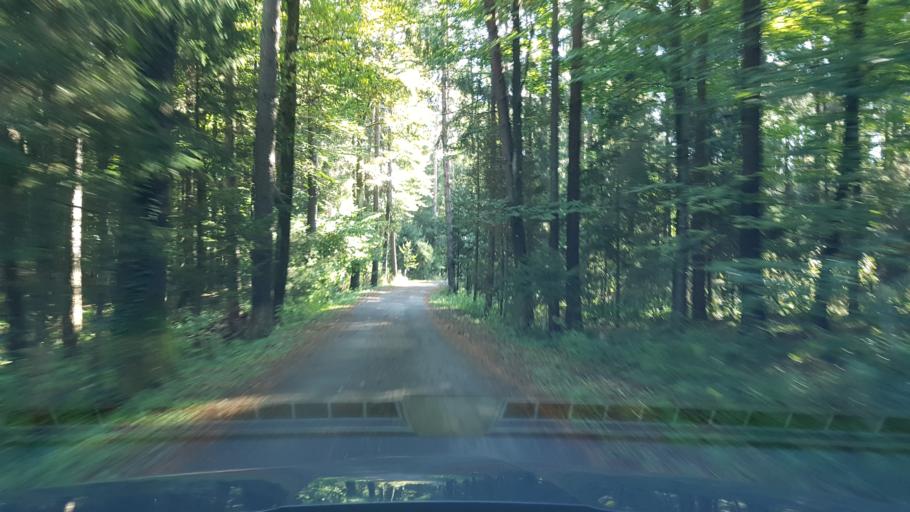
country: AT
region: Styria
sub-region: Politischer Bezirk Deutschlandsberg
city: Sankt Martin im Sulmtal
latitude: 46.7439
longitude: 15.2907
